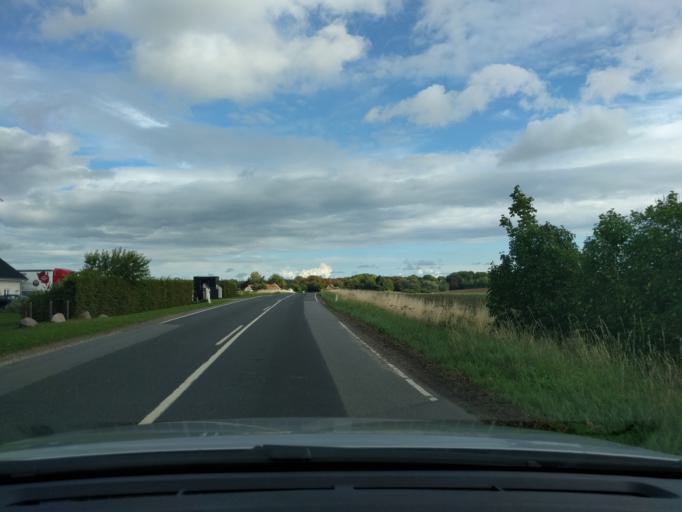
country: DK
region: South Denmark
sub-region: Nyborg Kommune
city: Ullerslev
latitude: 55.3981
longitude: 10.6662
